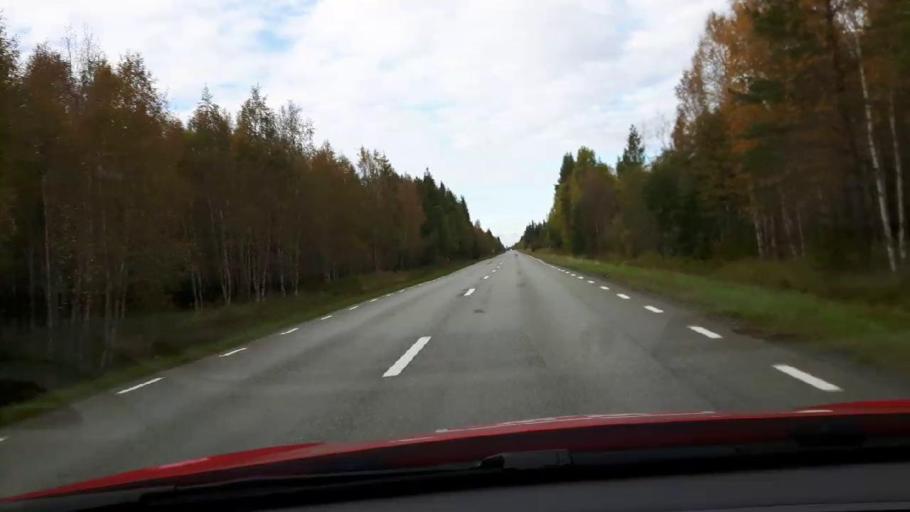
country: SE
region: Jaemtland
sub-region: Krokoms Kommun
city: Valla
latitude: 63.2256
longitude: 14.0171
